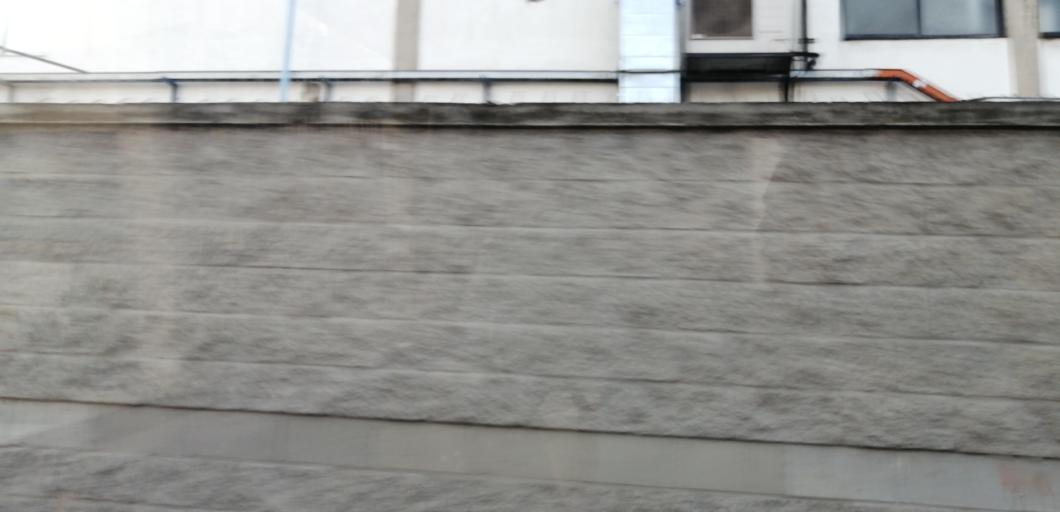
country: CO
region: Bogota D.C.
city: Bogota
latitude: 4.5944
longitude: -74.1486
